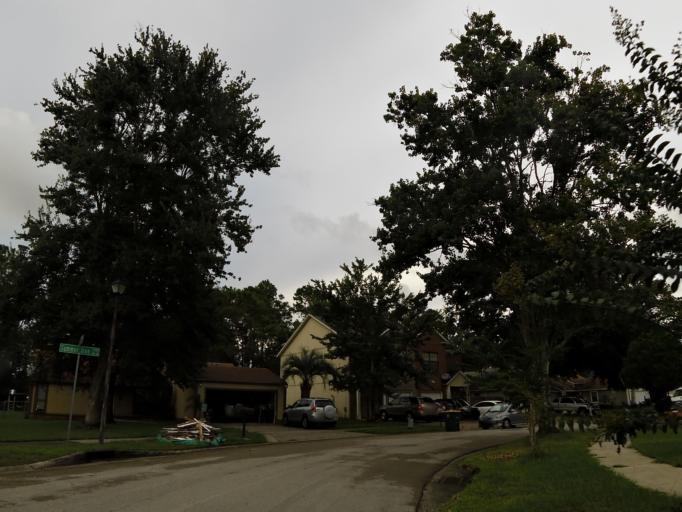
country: US
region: Florida
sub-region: Duval County
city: Neptune Beach
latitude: 30.3055
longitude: -81.5215
